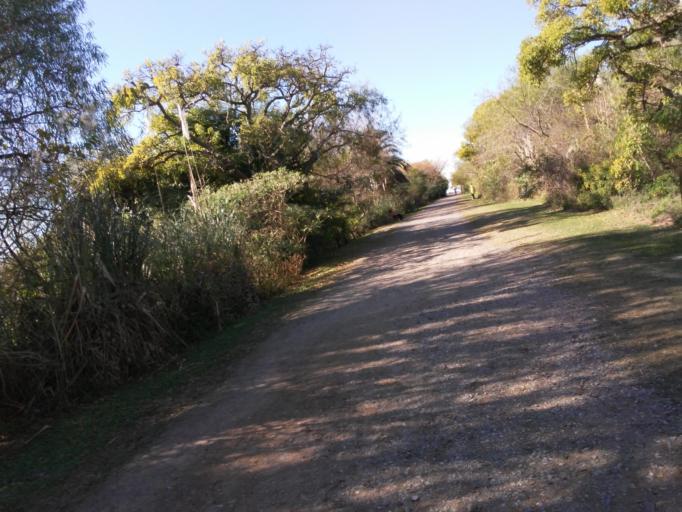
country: AR
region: Buenos Aires F.D.
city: Buenos Aires
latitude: -34.6071
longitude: -58.3496
